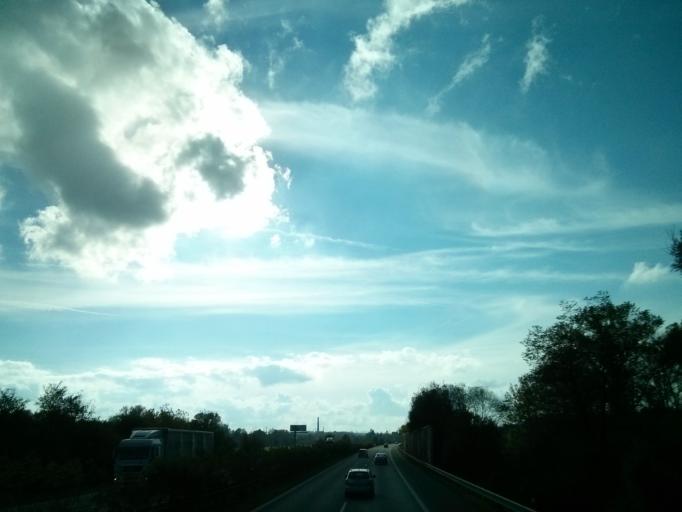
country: CZ
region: Central Bohemia
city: Zdice
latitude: 49.9158
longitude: 13.9954
